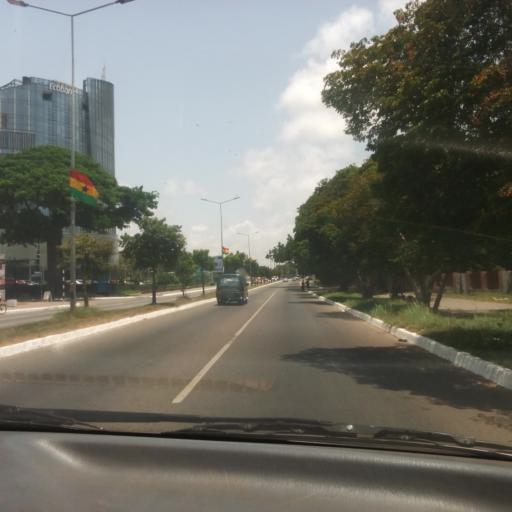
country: GH
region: Greater Accra
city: Accra
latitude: 5.5565
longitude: -0.1994
